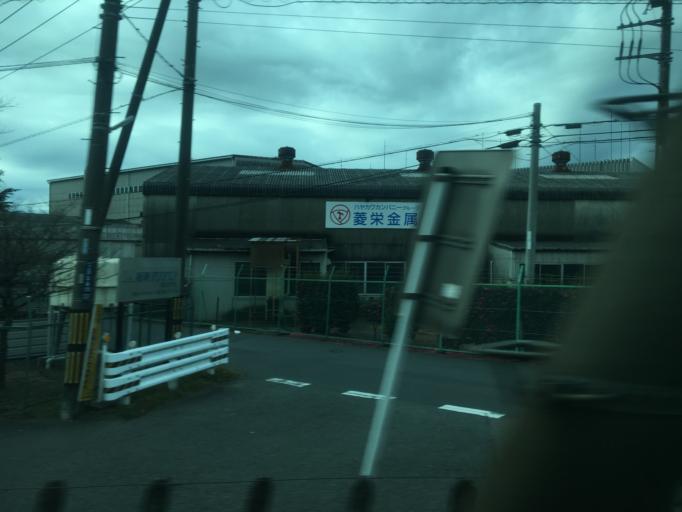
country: JP
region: Saitama
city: Okegawa
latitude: 36.0092
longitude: 139.5528
